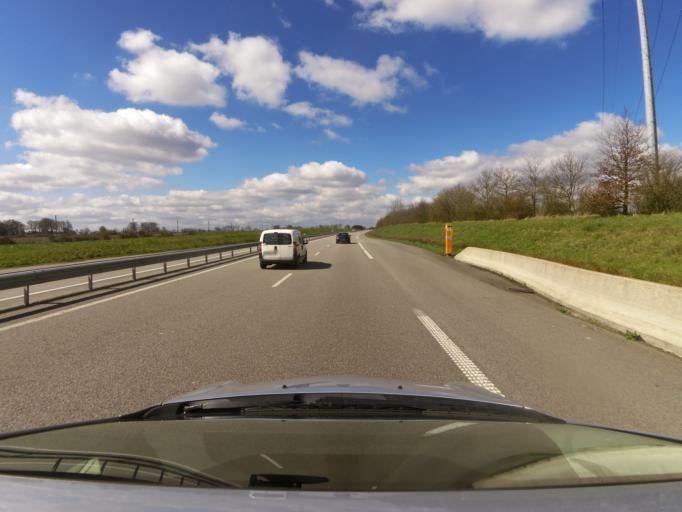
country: FR
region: Haute-Normandie
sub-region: Departement de la Seine-Maritime
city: Totes
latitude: 49.6382
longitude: 1.0323
